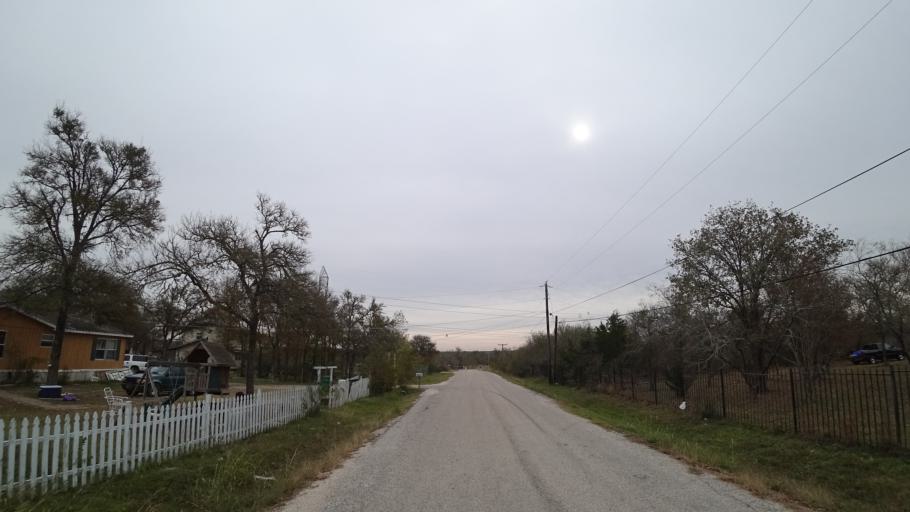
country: US
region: Texas
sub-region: Travis County
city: Garfield
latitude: 30.0974
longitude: -97.5730
